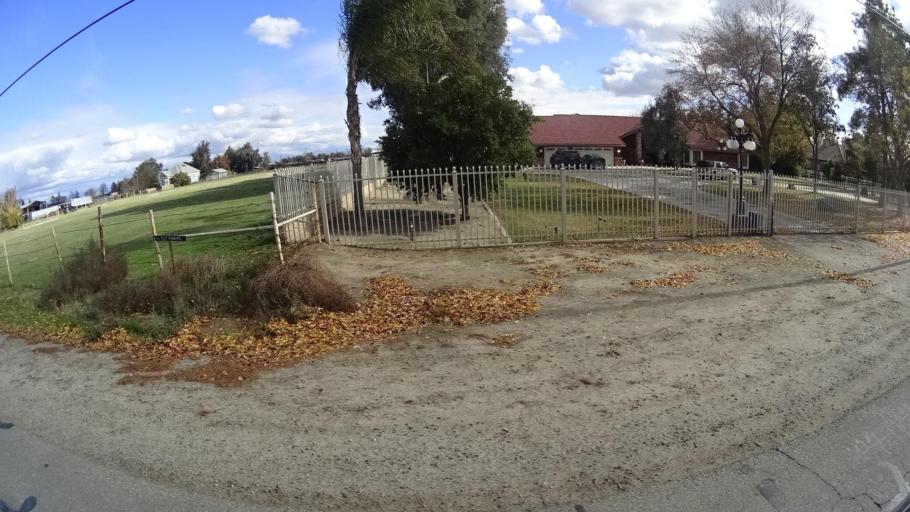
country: US
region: California
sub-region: Kern County
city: Greenfield
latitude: 35.2397
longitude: -119.0746
